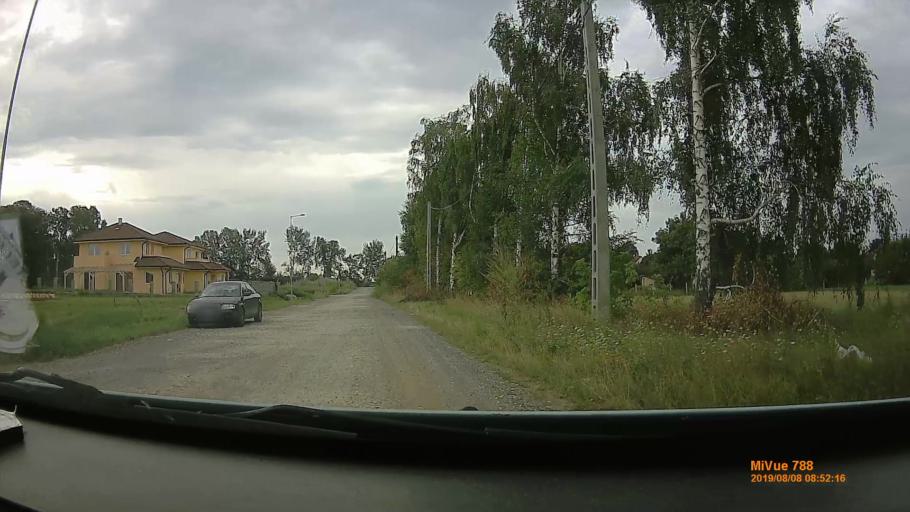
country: HU
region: Hajdu-Bihar
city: Debrecen
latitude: 47.5996
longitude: 21.6461
